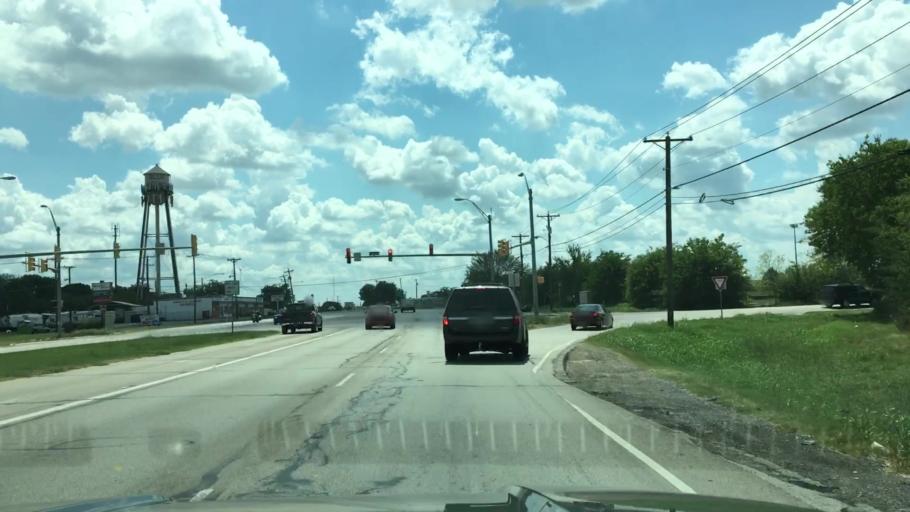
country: US
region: Texas
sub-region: Tarrant County
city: Blue Mound
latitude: 32.8621
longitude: -97.3428
